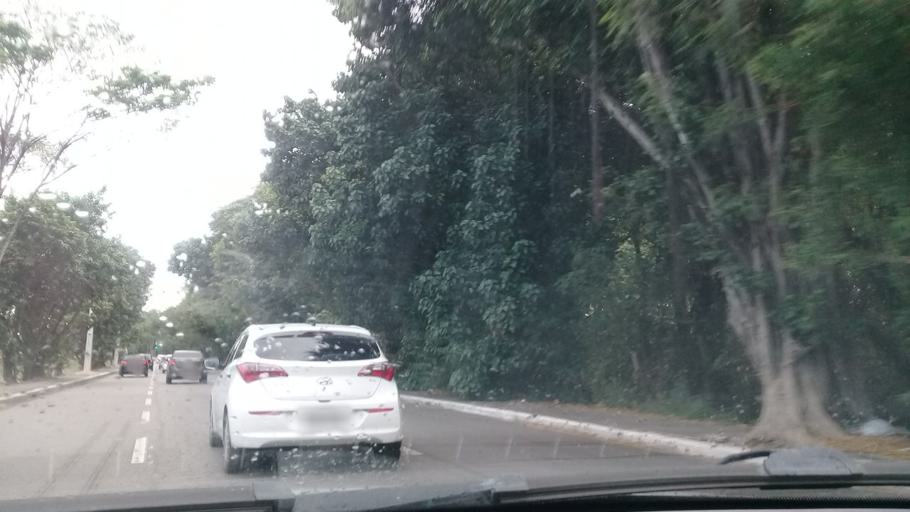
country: BR
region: Pernambuco
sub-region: Recife
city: Recife
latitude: -8.1193
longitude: -34.9084
